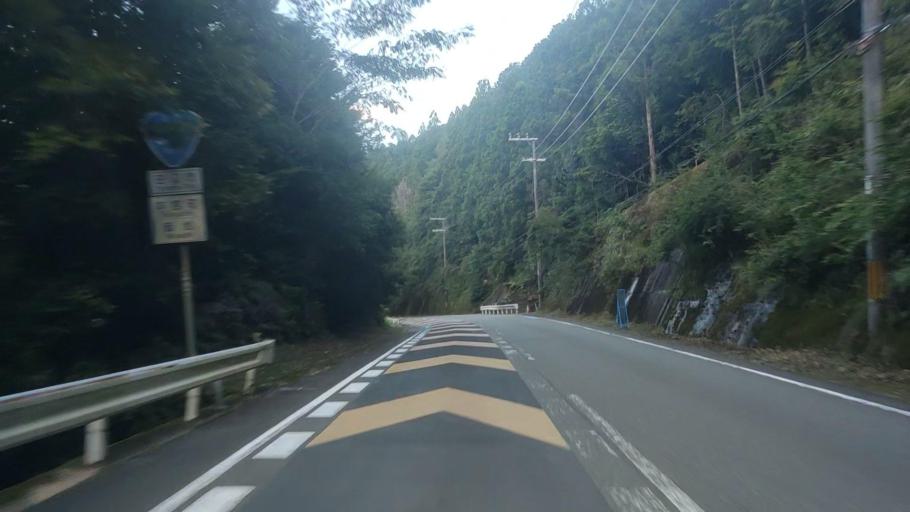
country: JP
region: Wakayama
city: Shingu
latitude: 33.8071
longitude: 135.7267
